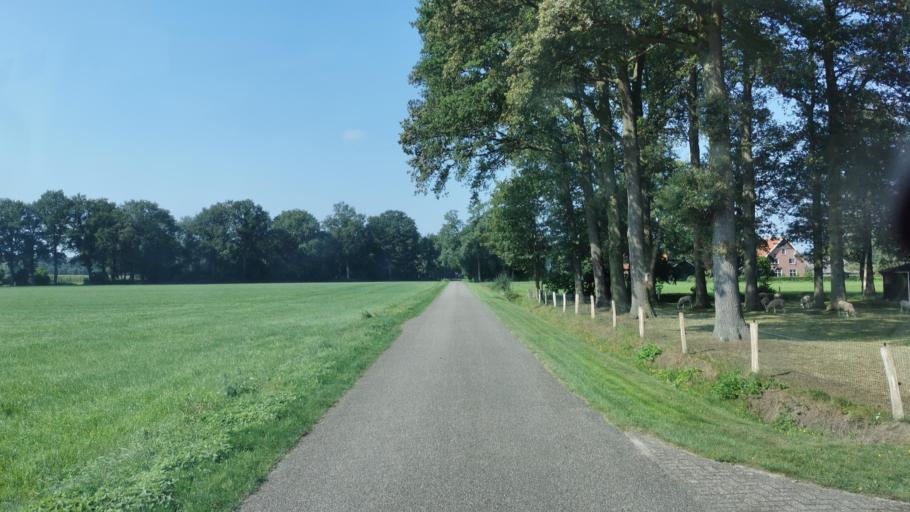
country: NL
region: Overijssel
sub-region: Gemeente Tubbergen
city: Tubbergen
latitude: 52.3696
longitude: 6.8034
